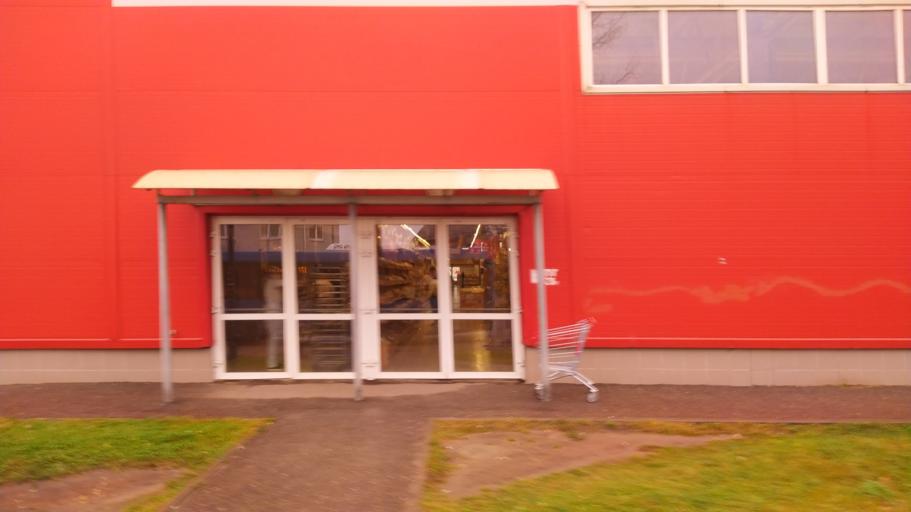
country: RU
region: Tverskaya
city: Tver
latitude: 56.8286
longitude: 35.8940
